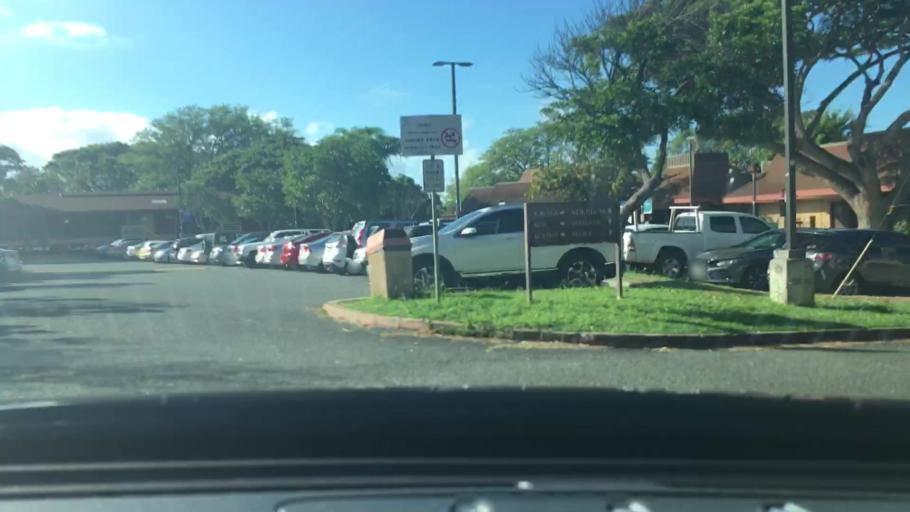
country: US
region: Hawaii
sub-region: Honolulu County
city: Honolulu
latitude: 21.2729
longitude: -157.8010
